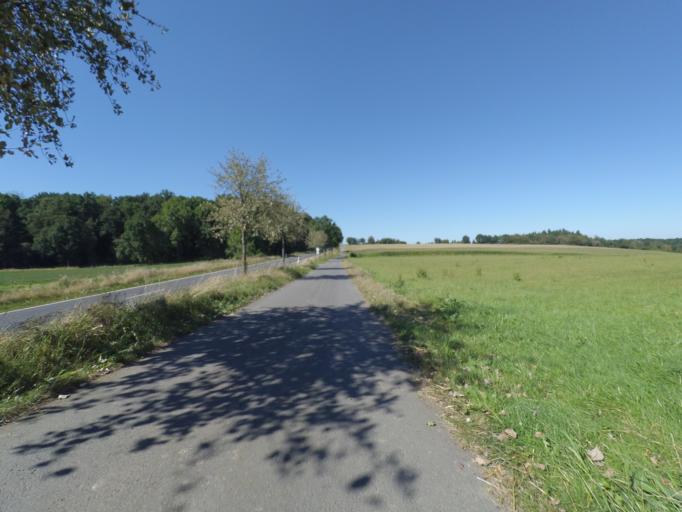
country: DE
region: Rheinland-Pfalz
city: Lutzerath
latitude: 50.1021
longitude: 7.0169
